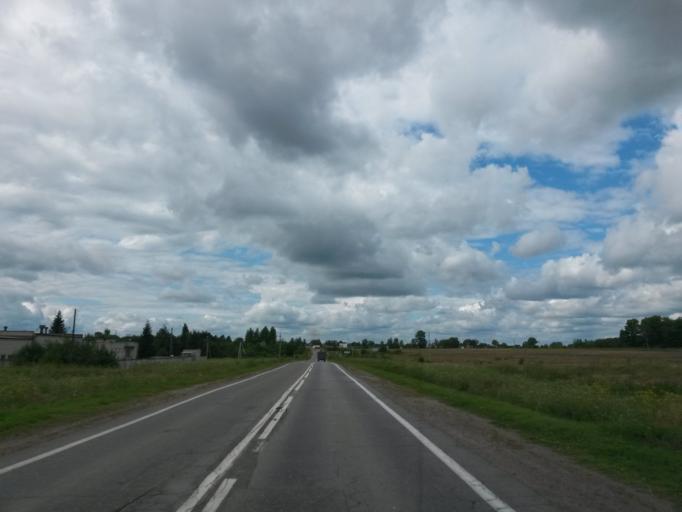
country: RU
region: Jaroslavl
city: Tutayev
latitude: 57.8775
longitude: 39.5732
